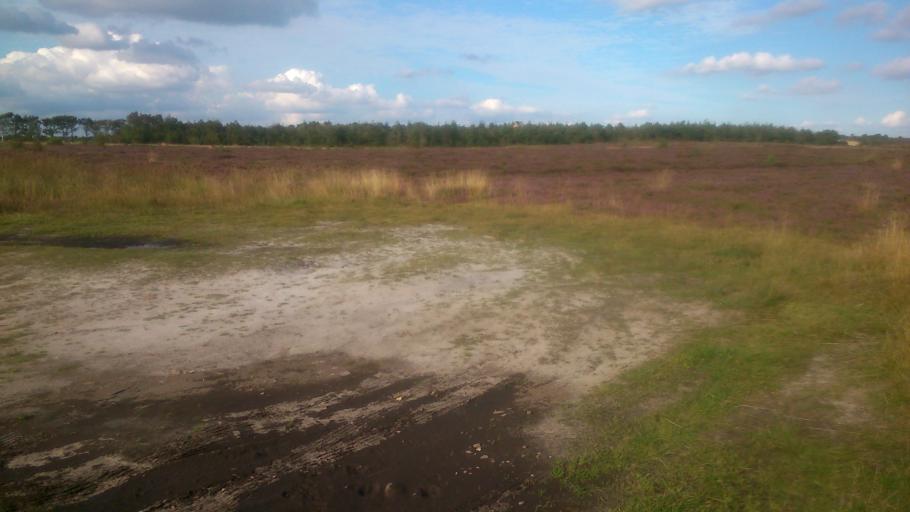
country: DK
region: Central Jutland
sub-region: Ringkobing-Skjern Kommune
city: Skjern
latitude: 56.0273
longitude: 8.4451
